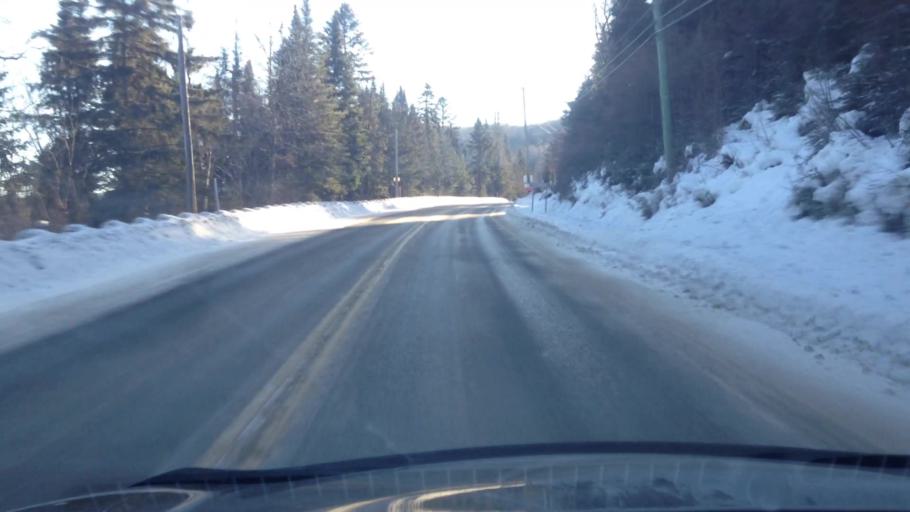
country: CA
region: Quebec
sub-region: Laurentides
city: Sainte-Agathe-des-Monts
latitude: 45.9178
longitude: -74.3753
